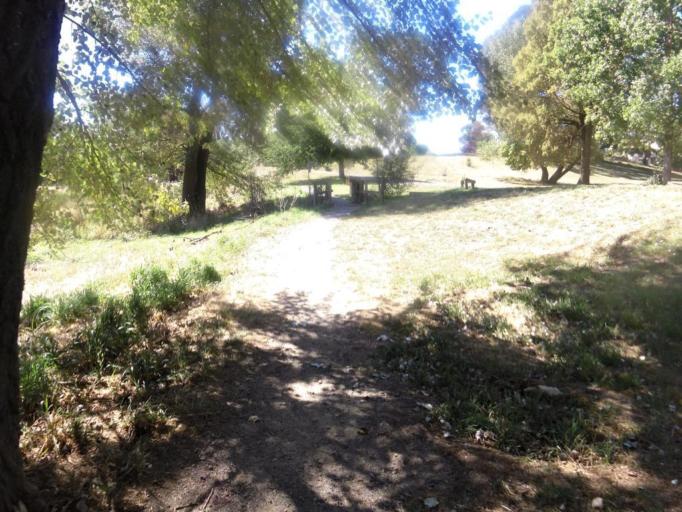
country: AU
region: Victoria
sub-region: Mount Alexander
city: Castlemaine
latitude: -37.2540
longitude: 144.4472
